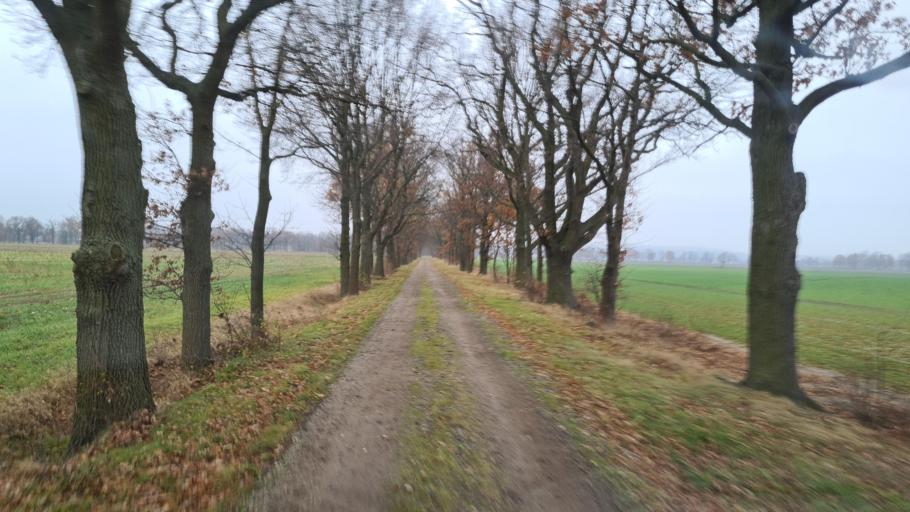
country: DE
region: Brandenburg
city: Schraden
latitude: 51.4125
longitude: 13.7051
